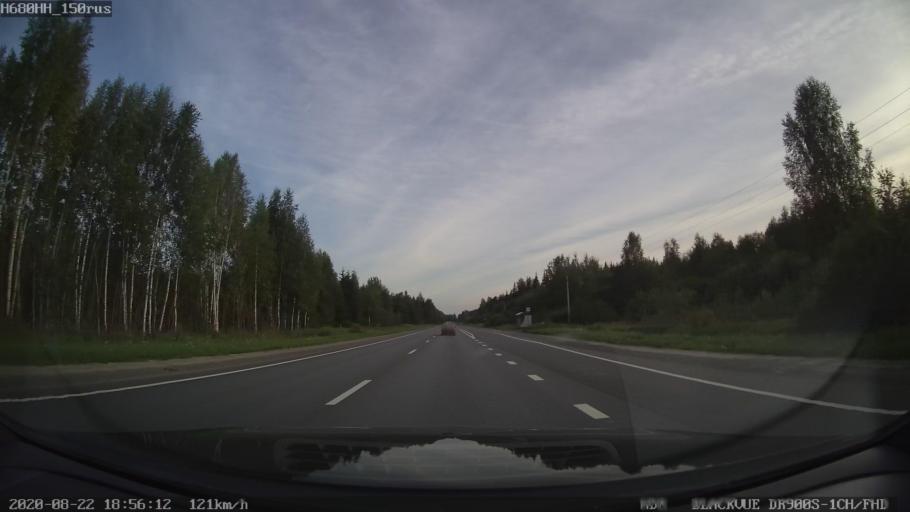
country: RU
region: Tverskaya
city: Rameshki
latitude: 57.1874
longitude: 36.0828
